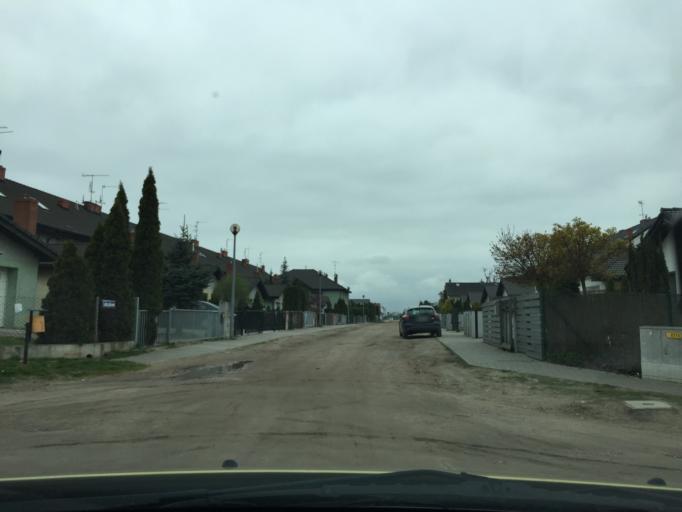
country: PL
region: Greater Poland Voivodeship
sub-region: Powiat poznanski
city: Plewiska
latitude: 52.3738
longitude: 16.8161
